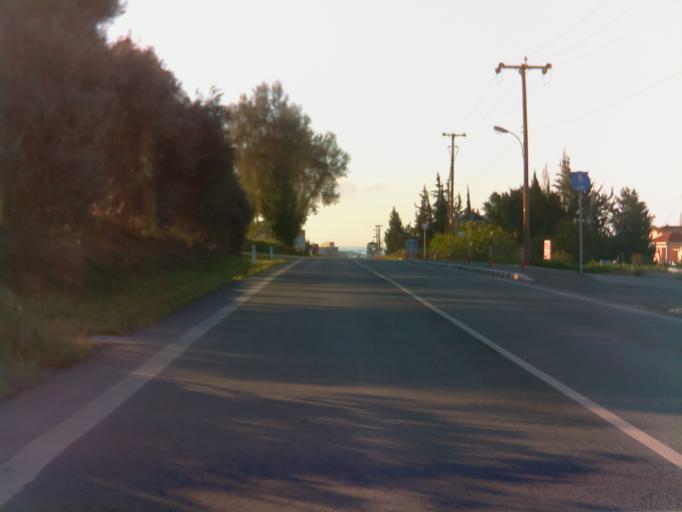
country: CY
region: Pafos
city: Kissonerga
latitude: 34.8282
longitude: 32.3923
